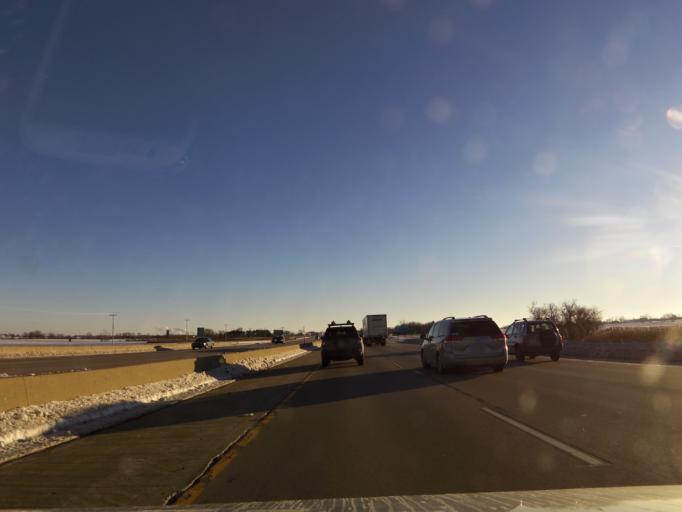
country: US
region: Wisconsin
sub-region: Kenosha County
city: Somers
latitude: 42.6533
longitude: -87.9529
